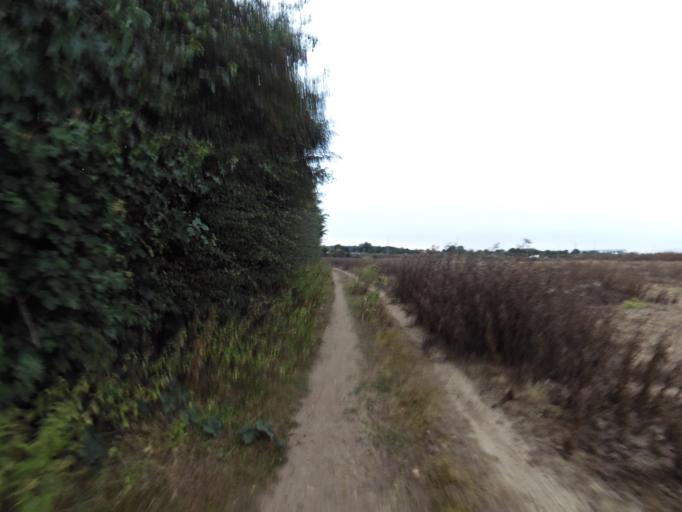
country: GB
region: England
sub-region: Hertfordshire
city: Radlett
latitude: 51.7140
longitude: -0.3134
